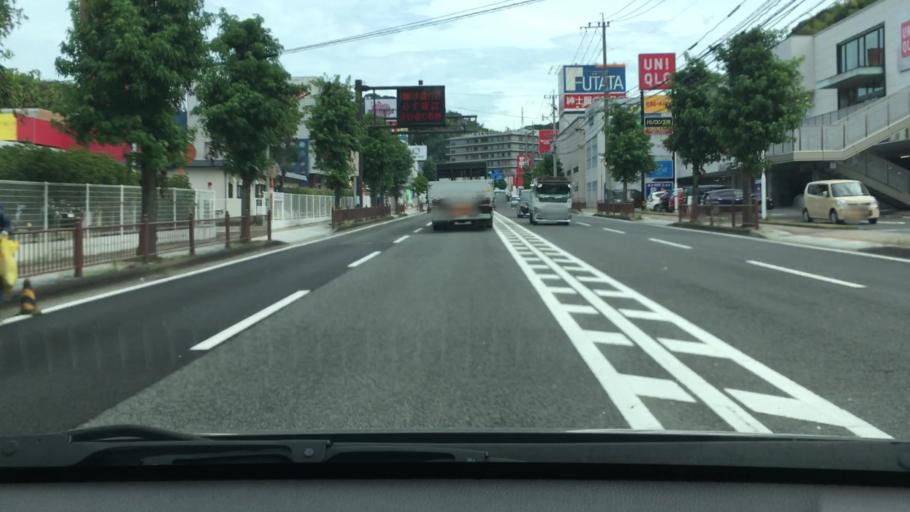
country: JP
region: Nagasaki
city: Togitsu
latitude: 32.8244
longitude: 129.8484
